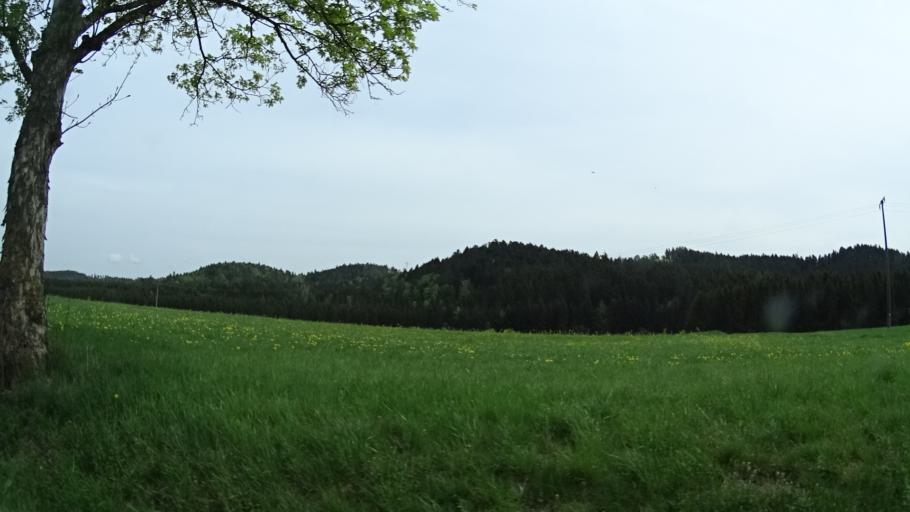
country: DE
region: Baden-Wuerttemberg
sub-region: Freiburg Region
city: Deisslingen
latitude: 48.0975
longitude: 8.5956
